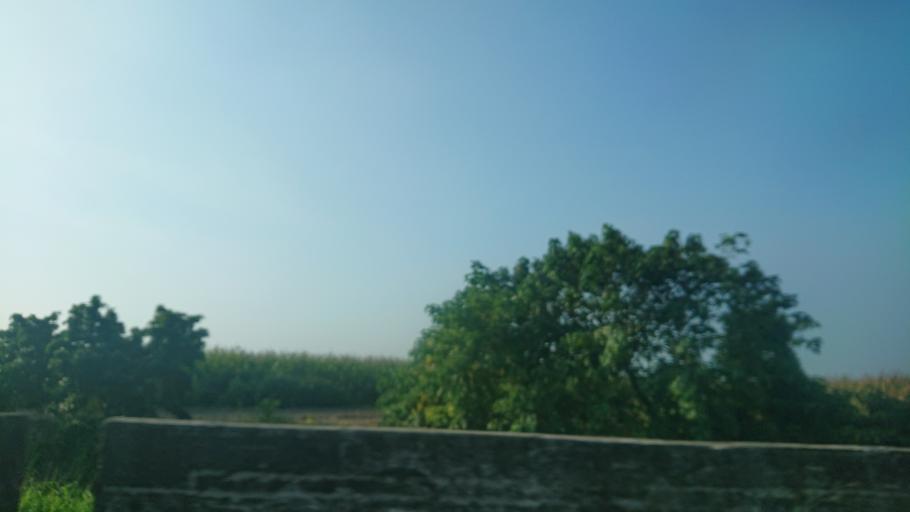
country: TW
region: Taiwan
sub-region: Tainan
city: Tainan
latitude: 23.1381
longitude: 120.2411
